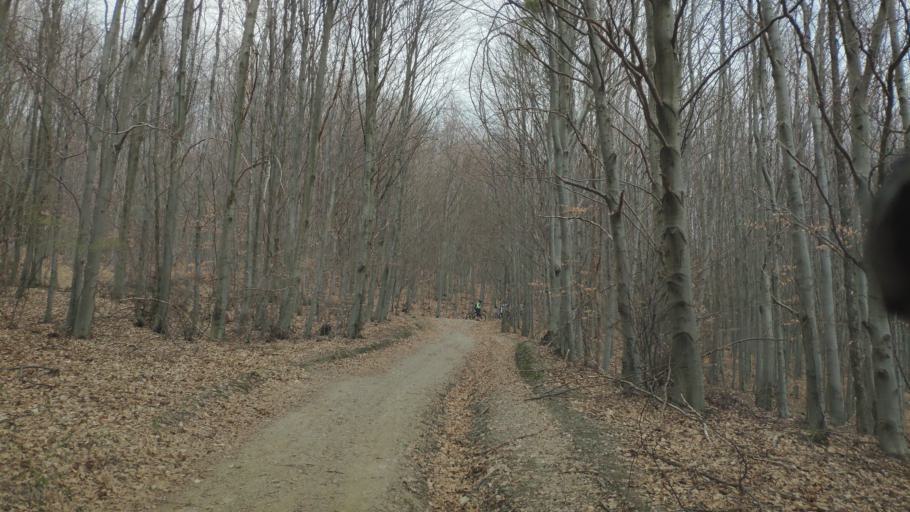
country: SK
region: Kosicky
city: Gelnica
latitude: 48.7559
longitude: 21.0214
